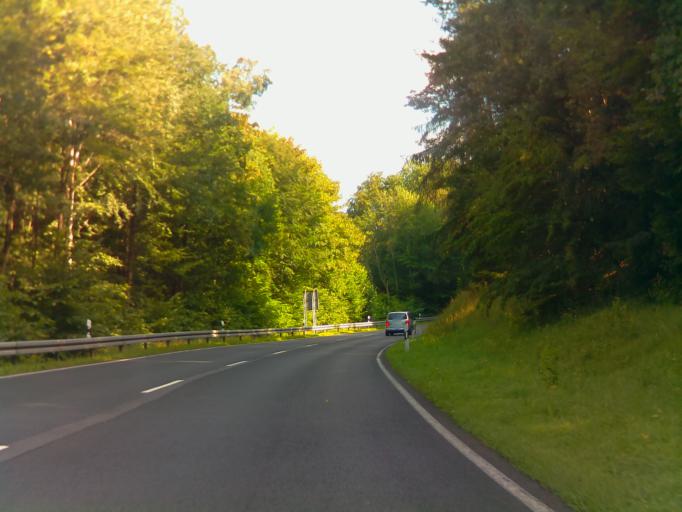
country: DE
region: Bavaria
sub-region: Regierungsbezirk Unterfranken
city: Riedenberg
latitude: 50.3142
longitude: 9.8414
